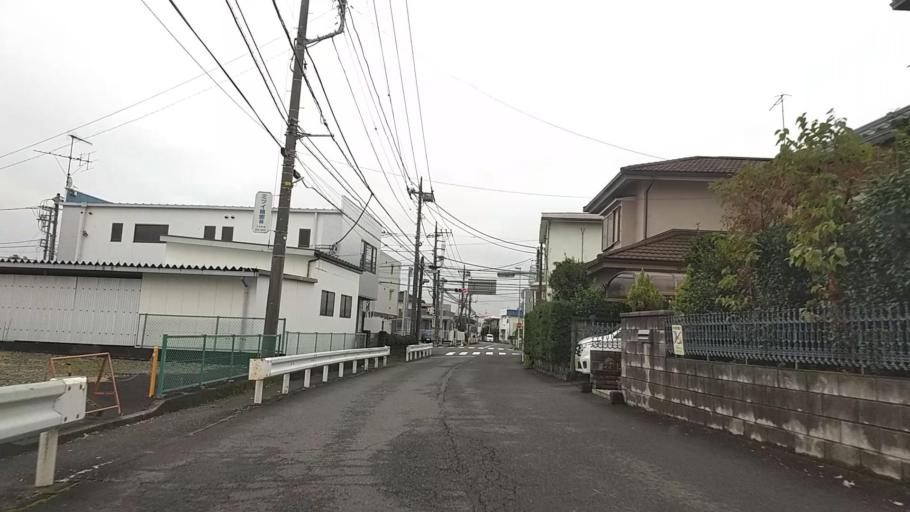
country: JP
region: Kanagawa
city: Atsugi
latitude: 35.4178
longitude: 139.3484
